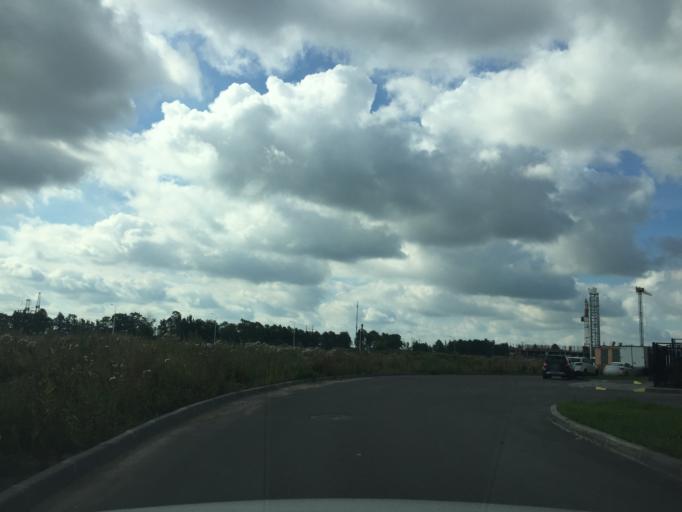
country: RU
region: St.-Petersburg
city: Pushkin
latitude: 59.7529
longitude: 30.3755
